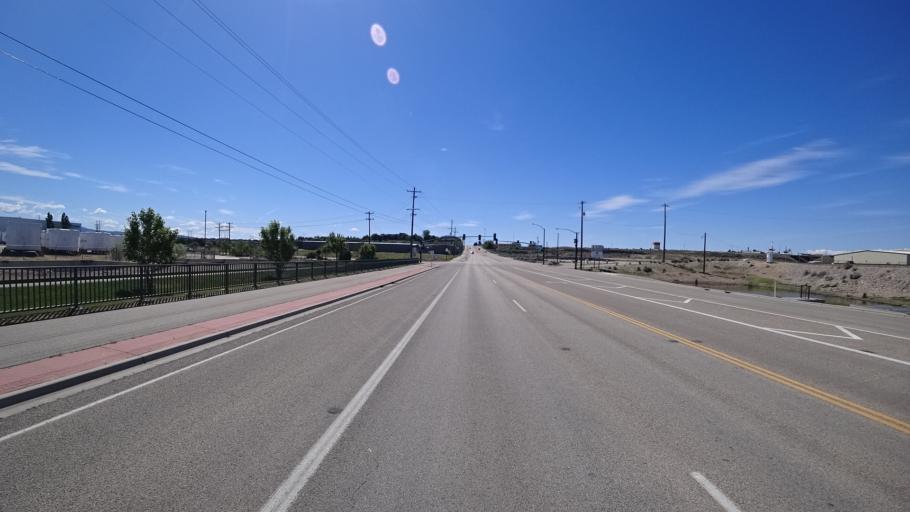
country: US
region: Idaho
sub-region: Ada County
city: Boise
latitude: 43.5504
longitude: -116.1603
